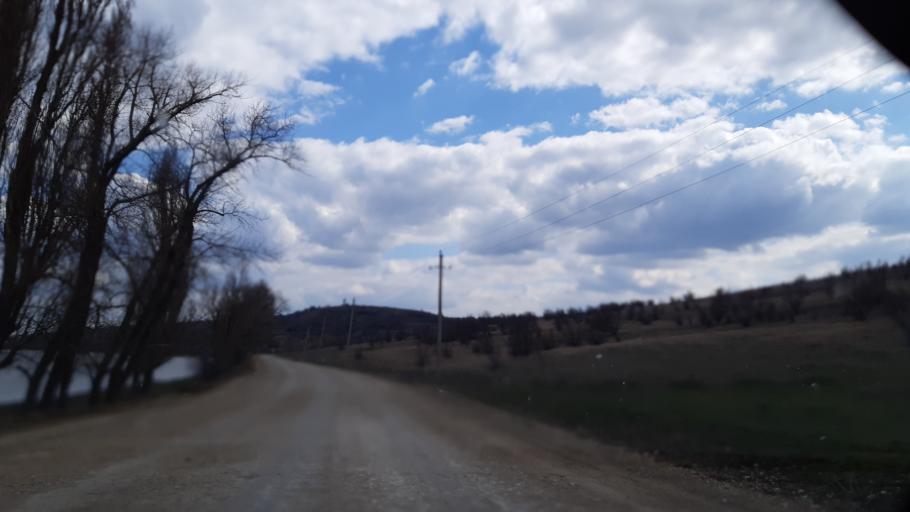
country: MD
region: Laloveni
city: Ialoveni
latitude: 46.8831
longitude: 28.7383
